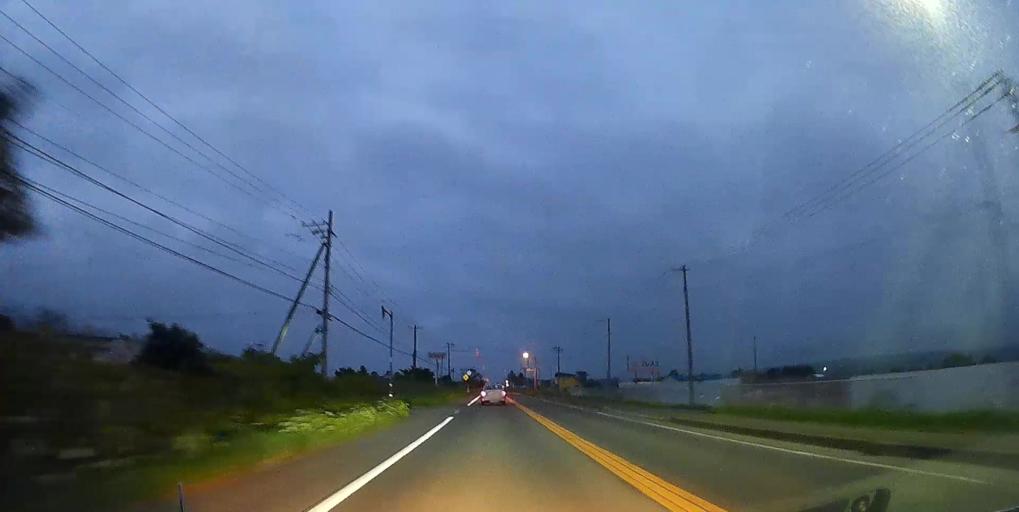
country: JP
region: Hokkaido
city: Nanae
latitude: 42.2209
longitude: 140.3738
